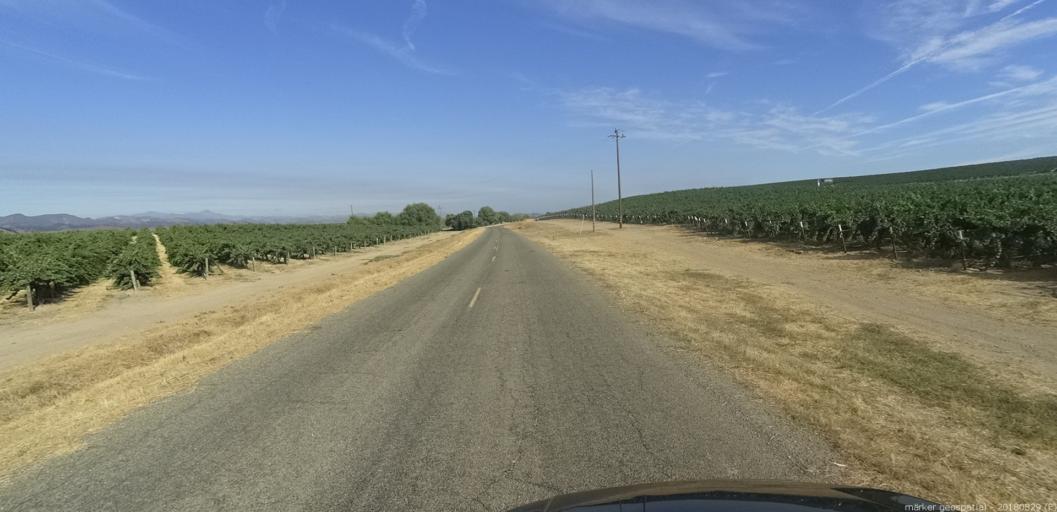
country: US
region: California
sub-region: Monterey County
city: King City
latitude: 36.0674
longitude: -120.9886
